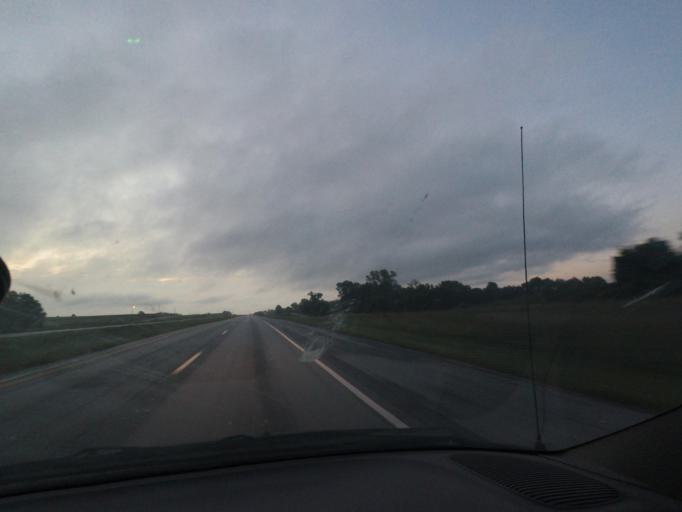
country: US
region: Missouri
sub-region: Linn County
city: Brookfield
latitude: 39.7631
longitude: -93.0263
